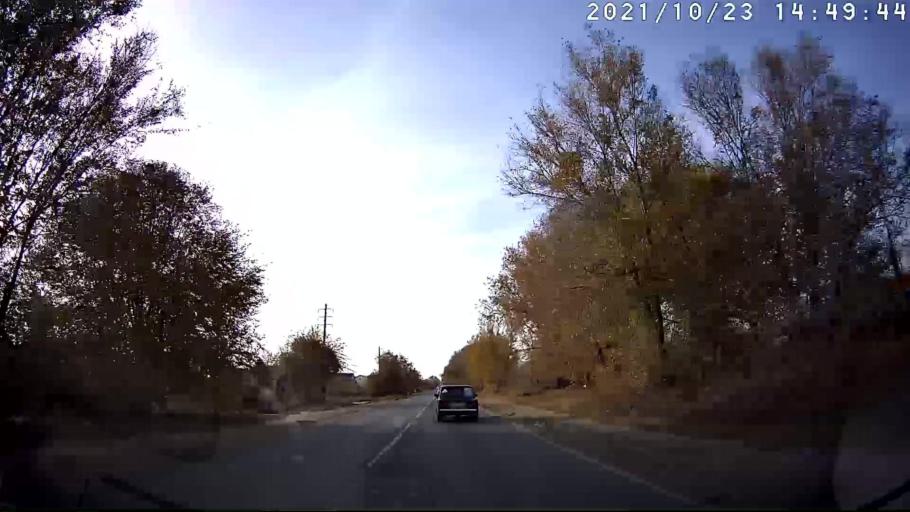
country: RU
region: Volgograd
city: Volgograd
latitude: 48.4281
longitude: 44.4798
